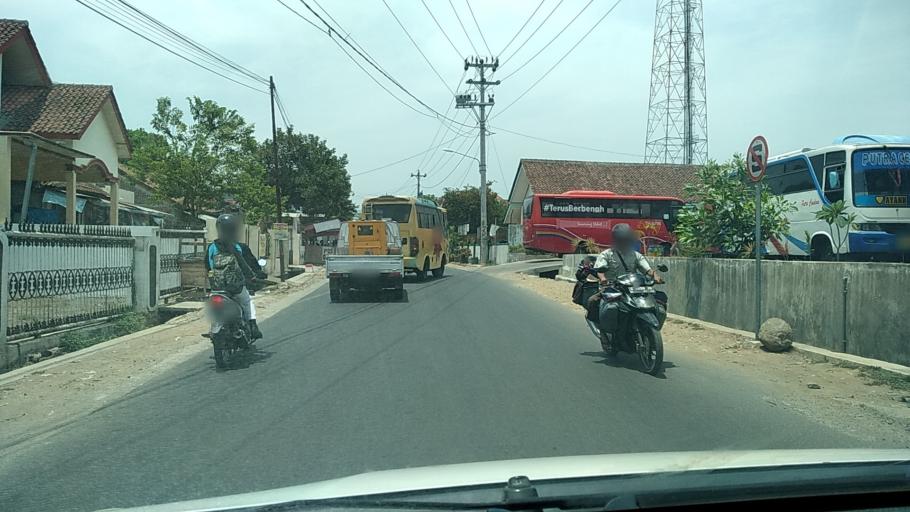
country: ID
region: Central Java
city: Ungaran
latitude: -7.0882
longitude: 110.3084
